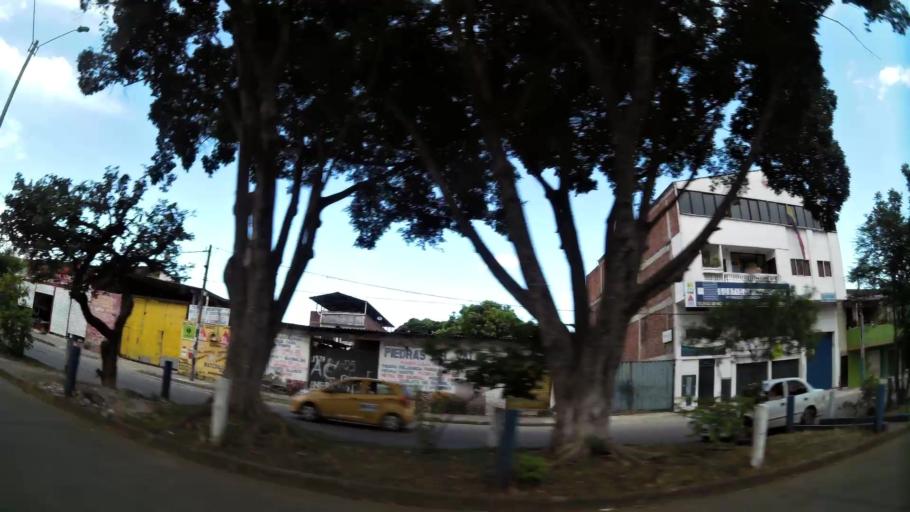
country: CO
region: Valle del Cauca
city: Cali
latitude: 3.4383
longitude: -76.5262
